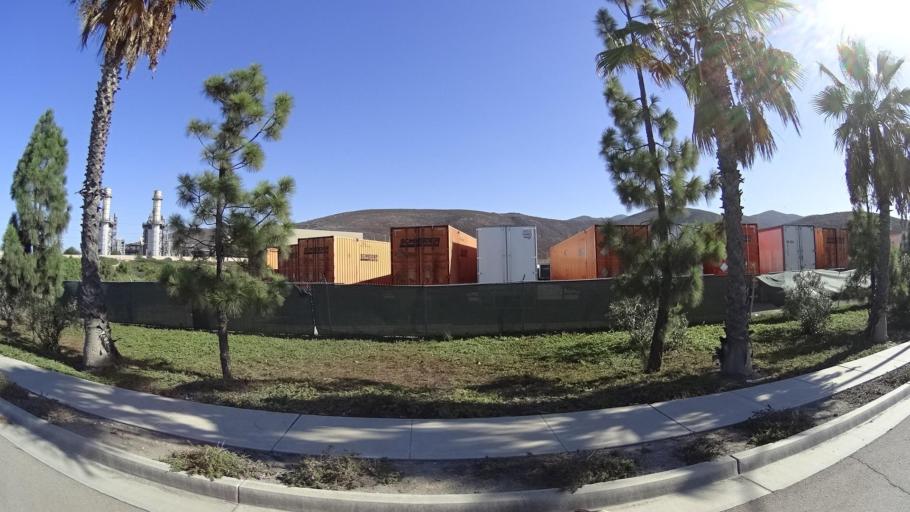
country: MX
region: Baja California
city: Tijuana
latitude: 32.5702
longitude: -116.9139
